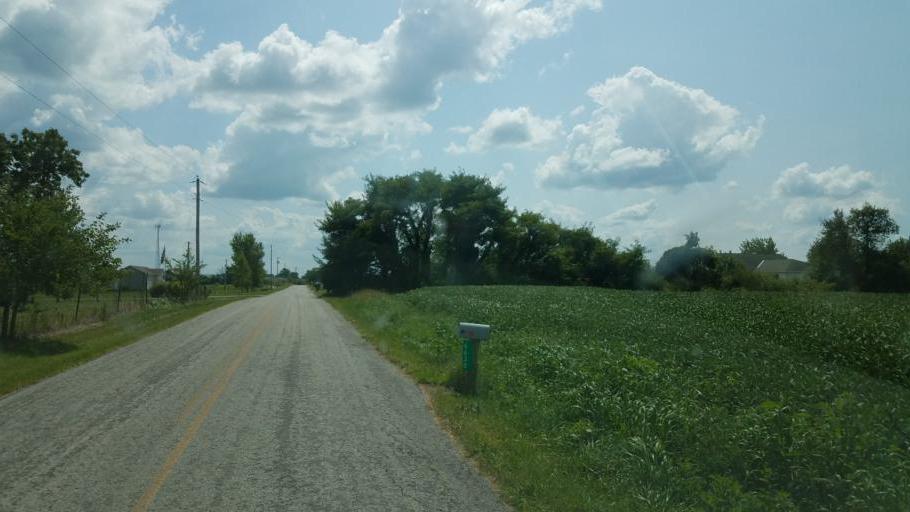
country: US
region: Ohio
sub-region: Delaware County
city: Ashley
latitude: 40.3441
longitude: -82.8797
